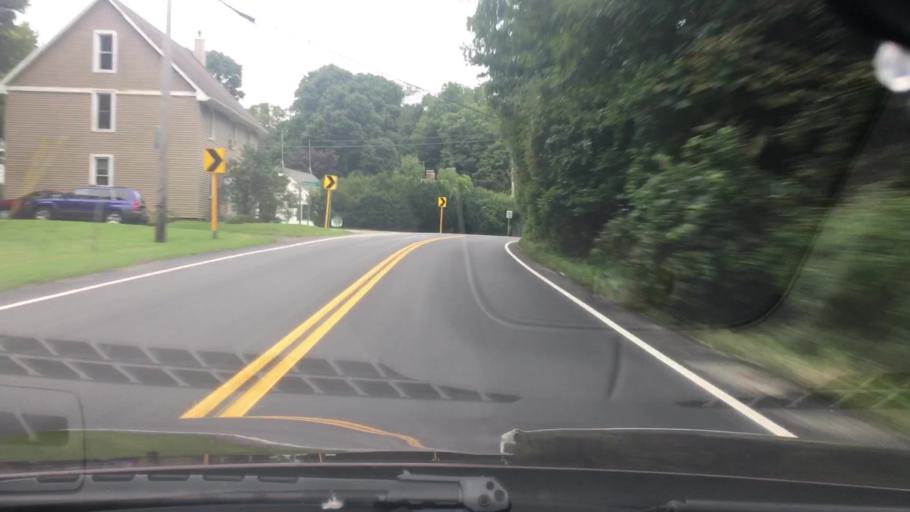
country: US
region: New York
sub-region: Dutchess County
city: Millbrook
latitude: 41.8256
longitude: -73.6202
